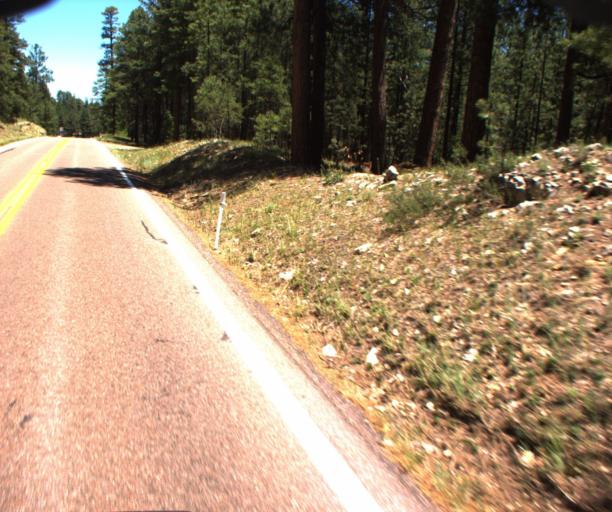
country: US
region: Arizona
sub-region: Gila County
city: Pine
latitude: 34.5427
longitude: -111.3252
